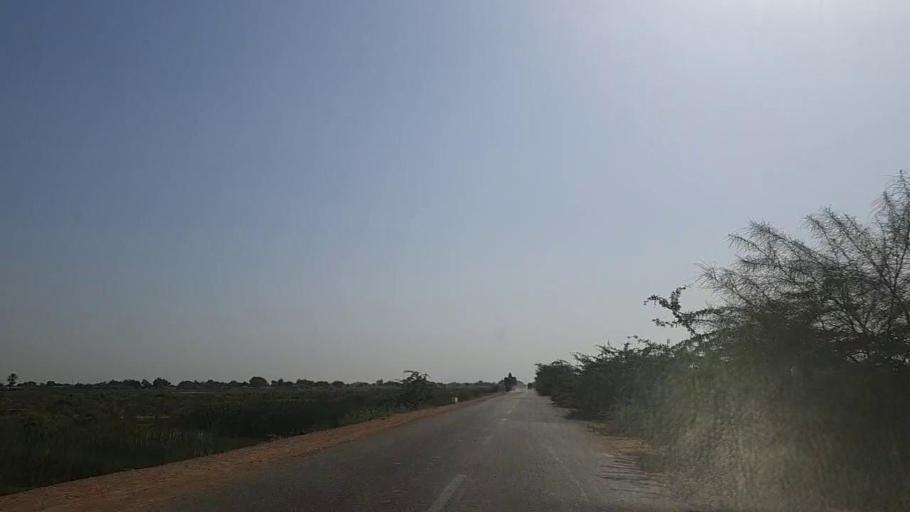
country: PK
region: Sindh
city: Mirpur Batoro
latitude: 24.5826
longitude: 68.2898
